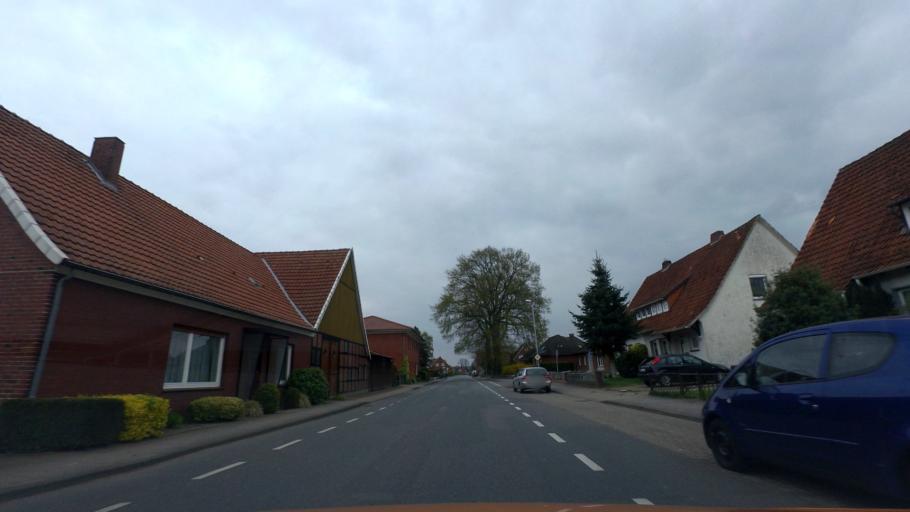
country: DE
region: Lower Saxony
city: Quakenbruck
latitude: 52.6819
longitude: 7.9628
